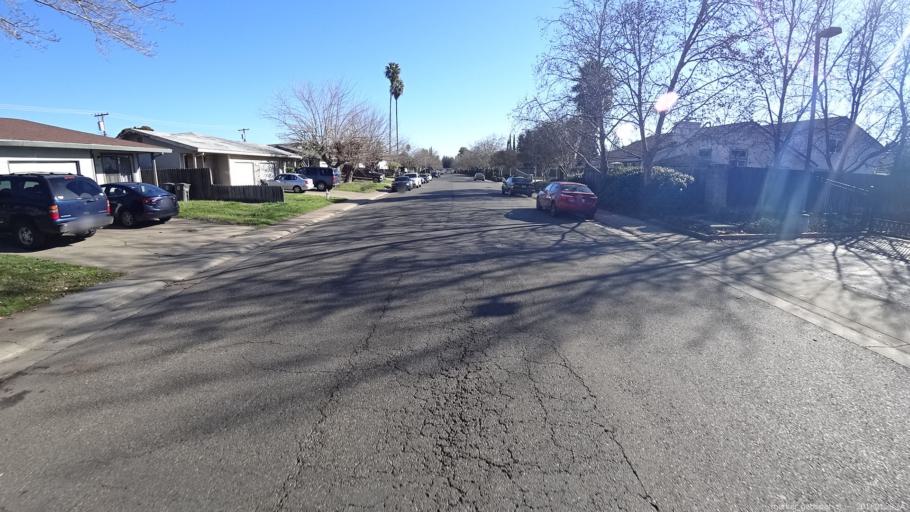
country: US
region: California
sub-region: Sacramento County
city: Rancho Cordova
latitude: 38.5688
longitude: -121.3147
